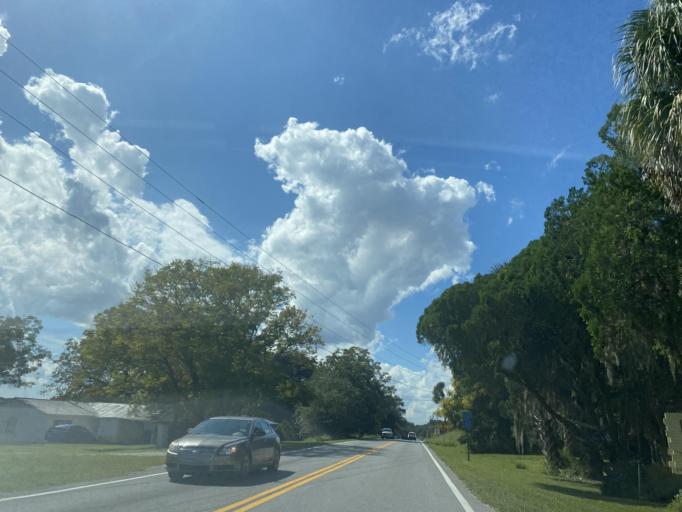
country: US
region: Florida
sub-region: Sumter County
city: The Villages
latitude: 28.9820
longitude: -81.9210
